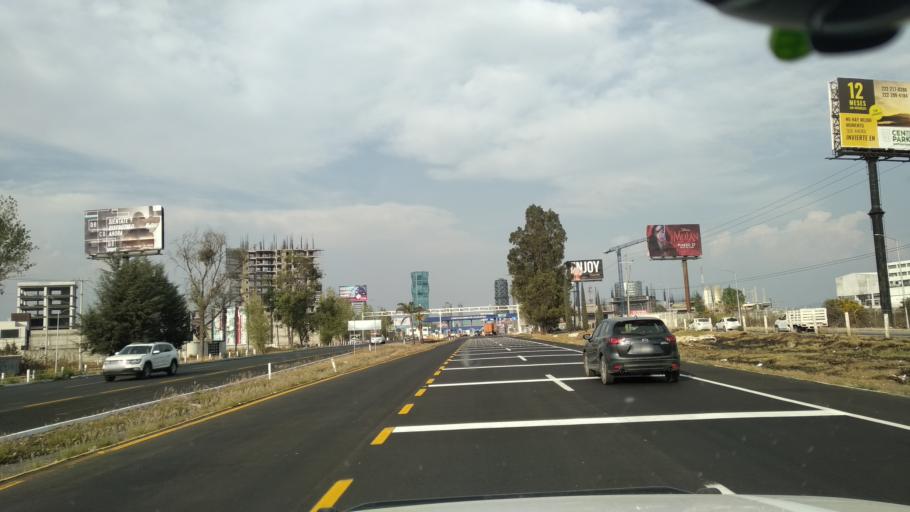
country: MX
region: Puebla
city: Tlazcalancingo
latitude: 19.0025
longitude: -98.2750
